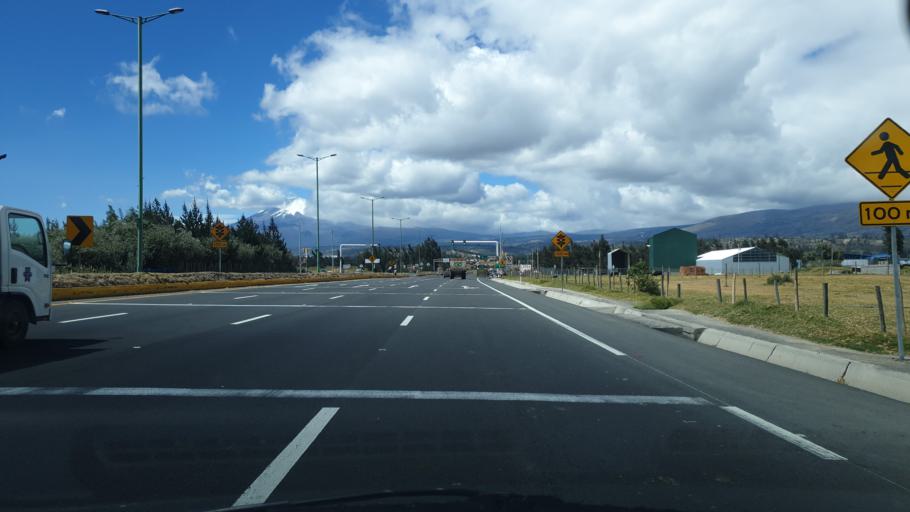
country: EC
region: Cotopaxi
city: Saquisili
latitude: -0.8723
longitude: -78.6387
